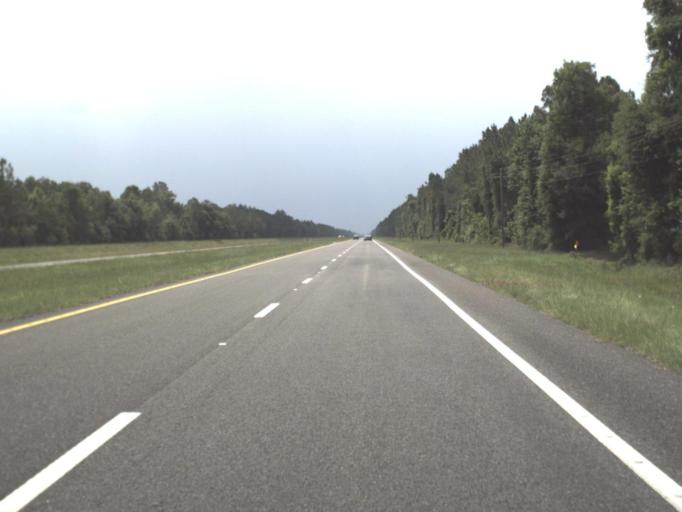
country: US
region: Florida
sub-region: Levy County
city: Chiefland
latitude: 29.3844
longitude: -82.8035
